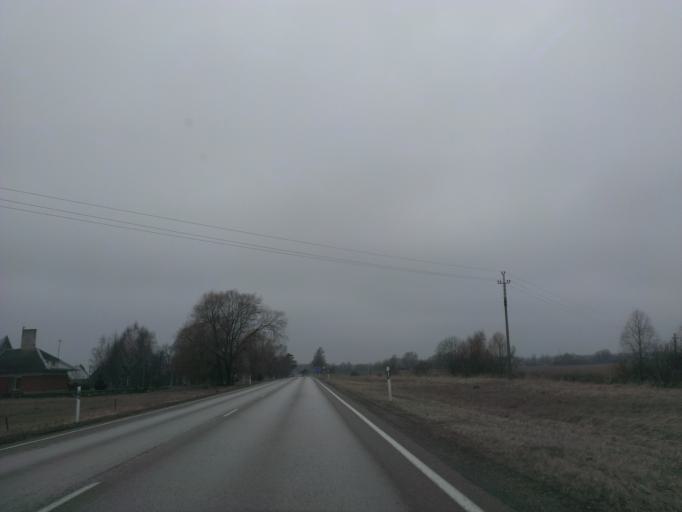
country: EE
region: Paernumaa
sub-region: Audru vald
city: Audru
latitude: 58.4693
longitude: 24.2005
